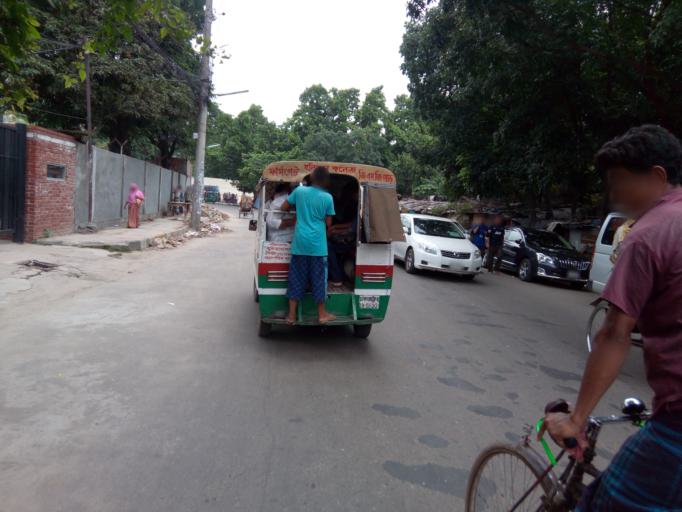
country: BD
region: Dhaka
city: Paltan
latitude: 23.7651
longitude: 90.4061
